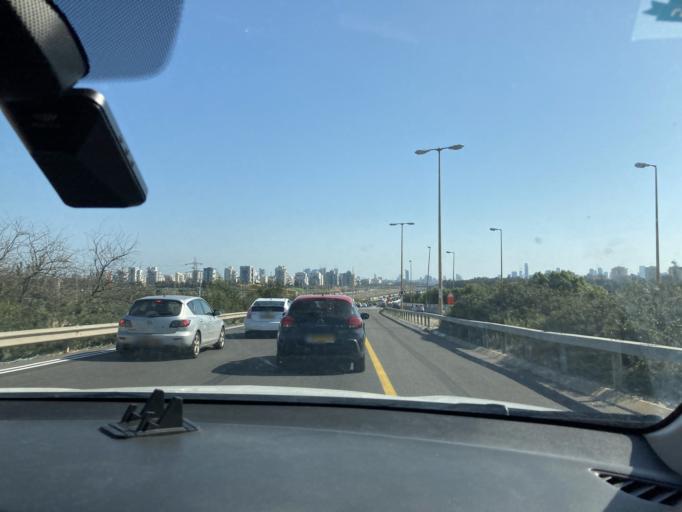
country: IL
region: Tel Aviv
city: Ramat HaSharon
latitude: 32.1390
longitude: 34.8090
